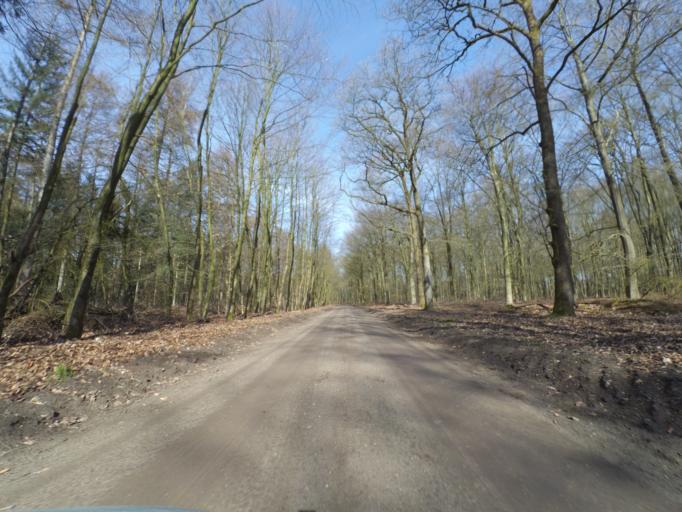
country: NL
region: Gelderland
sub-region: Gemeente Barneveld
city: Garderen
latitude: 52.2154
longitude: 5.7362
